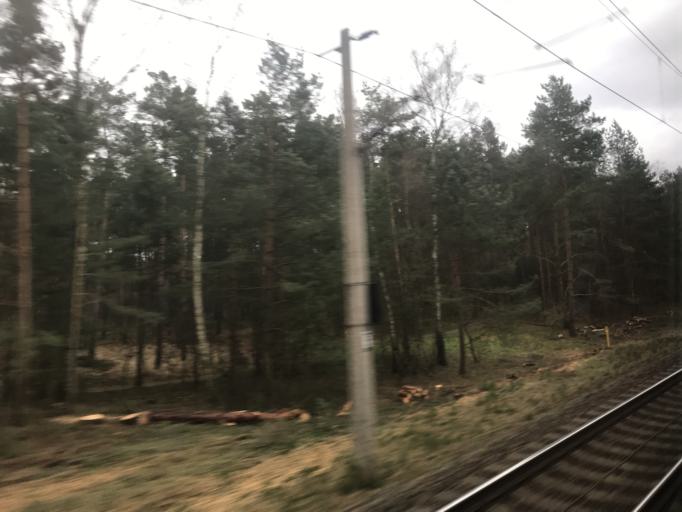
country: DE
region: Lower Saxony
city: Meinersen
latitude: 52.4562
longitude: 10.3619
